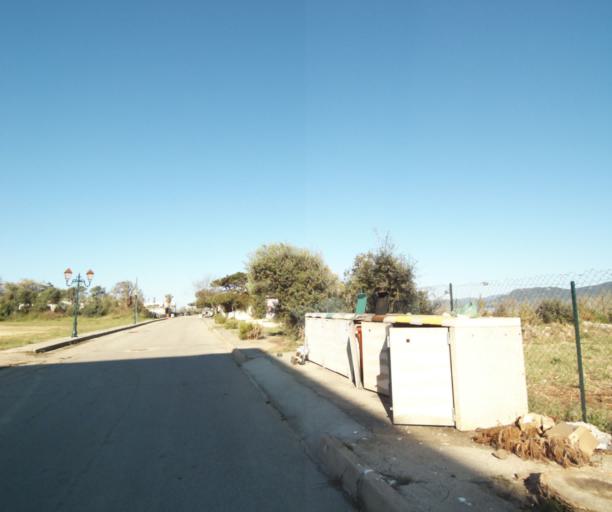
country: FR
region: Corsica
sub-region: Departement de la Corse-du-Sud
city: Propriano
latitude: 41.6750
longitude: 8.8966
